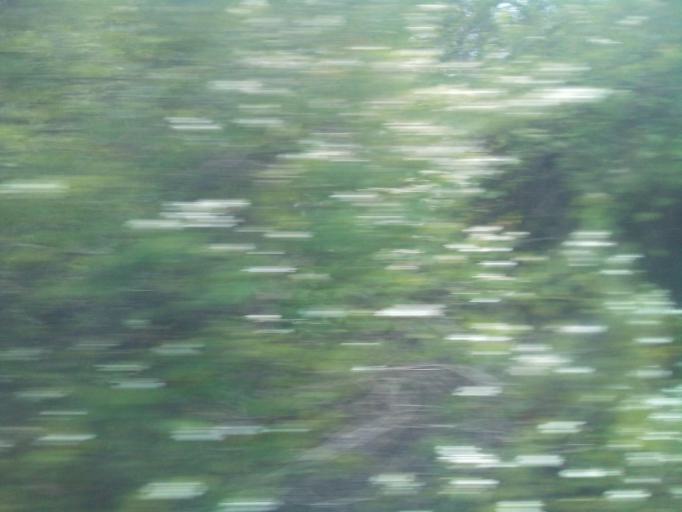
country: BR
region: Maranhao
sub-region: Santa Ines
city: Santa Ines
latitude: -3.6465
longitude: -45.7179
